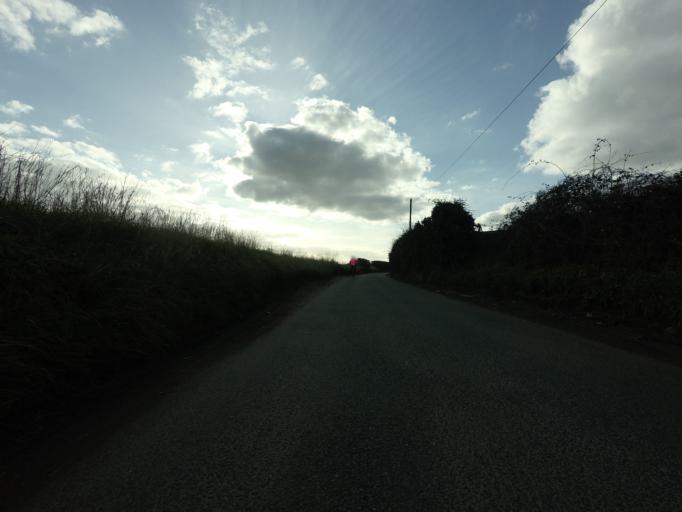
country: GB
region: England
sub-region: Kent
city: Dartford
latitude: 51.4222
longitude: 0.2144
